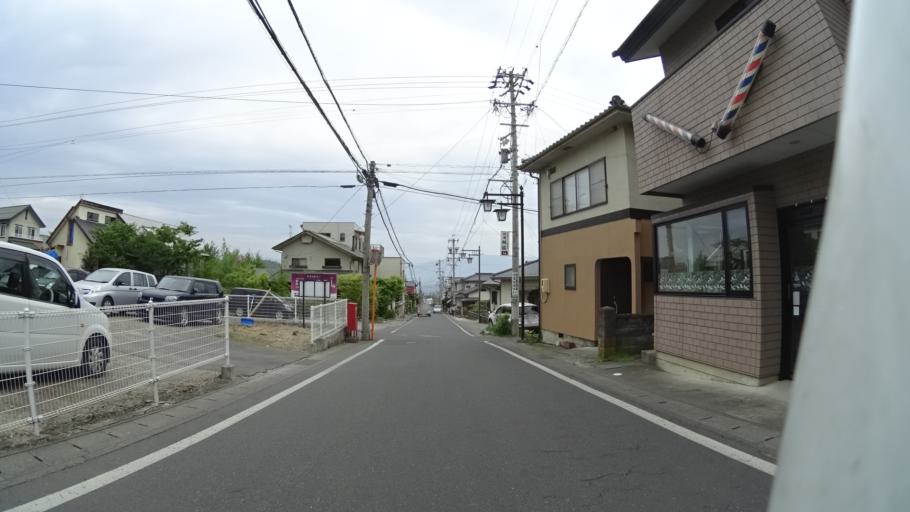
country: JP
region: Nagano
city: Kamimaruko
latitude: 36.3511
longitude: 138.1573
